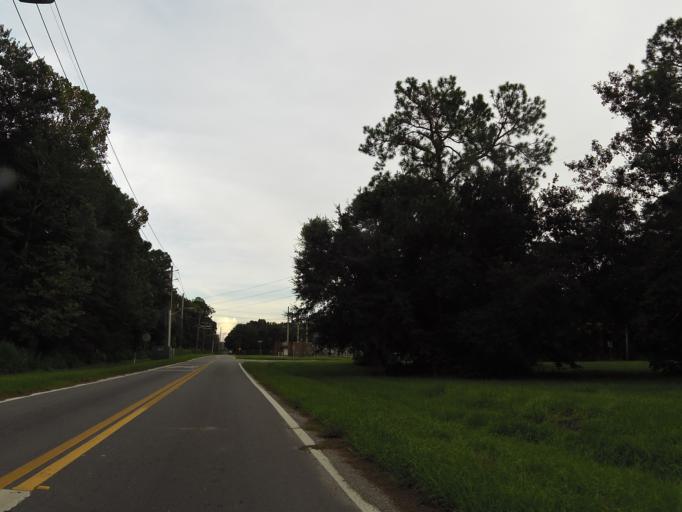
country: US
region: Florida
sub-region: Duval County
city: Jacksonville
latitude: 30.3567
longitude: -81.7171
